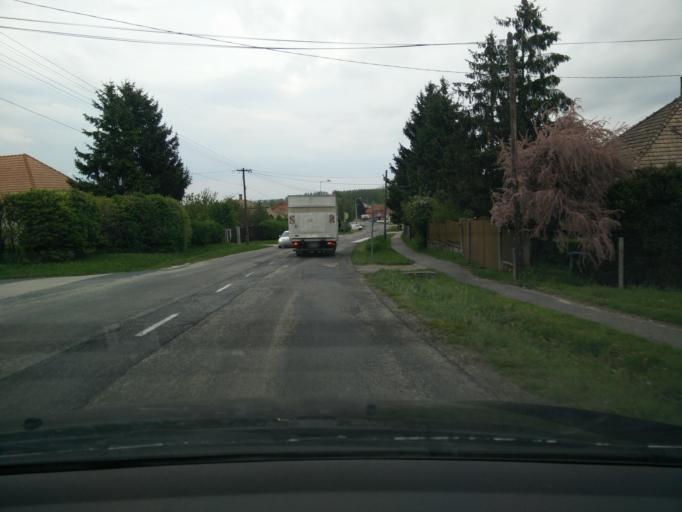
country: HU
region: Gyor-Moson-Sopron
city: Gyorszemere
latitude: 47.5527
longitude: 17.5620
